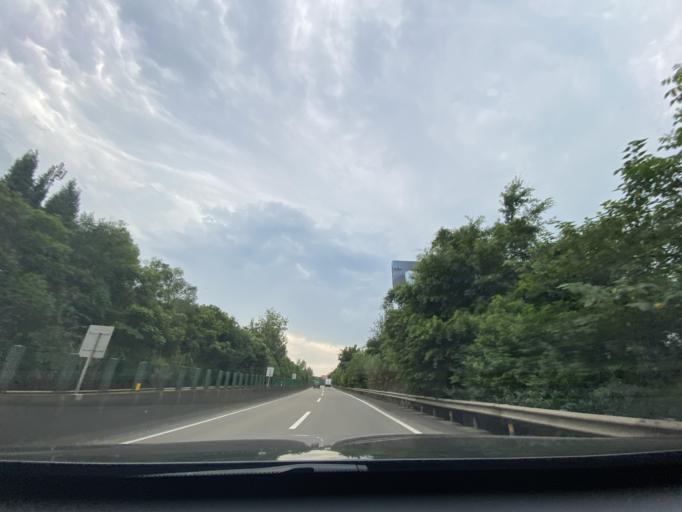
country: CN
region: Sichuan
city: Chonglong
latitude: 29.7158
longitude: 104.9402
